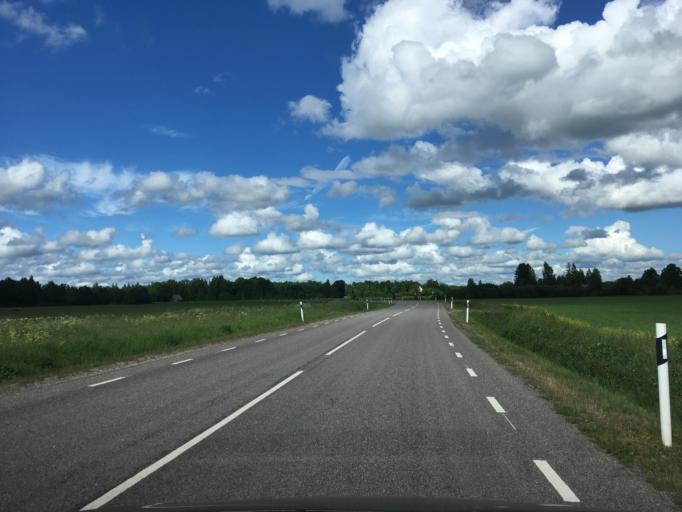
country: EE
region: Paernumaa
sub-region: Halinga vald
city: Parnu-Jaagupi
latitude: 58.6370
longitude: 24.5493
